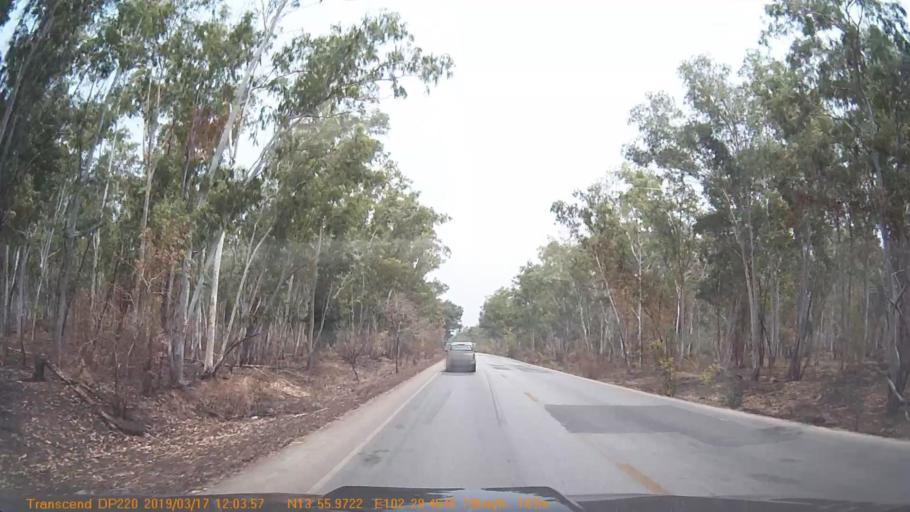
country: TH
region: Sa Kaeo
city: Khok Sung
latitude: 13.9331
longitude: 102.4913
